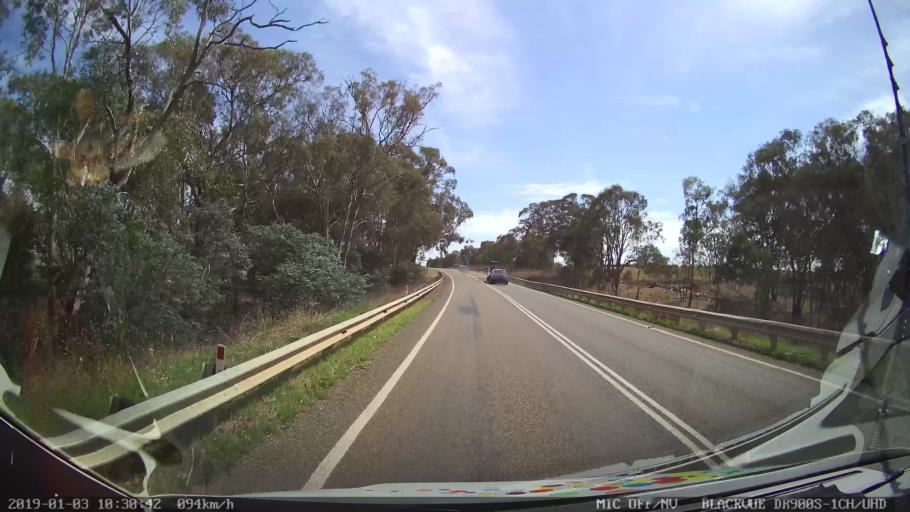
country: AU
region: New South Wales
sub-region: Young
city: Young
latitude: -34.3592
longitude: 148.2711
